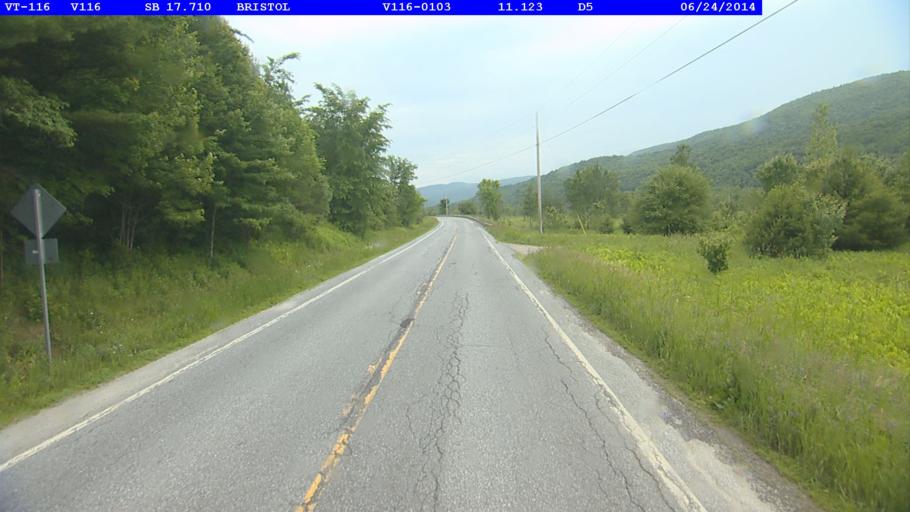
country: US
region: Vermont
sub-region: Addison County
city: Bristol
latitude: 44.1692
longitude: -73.0559
